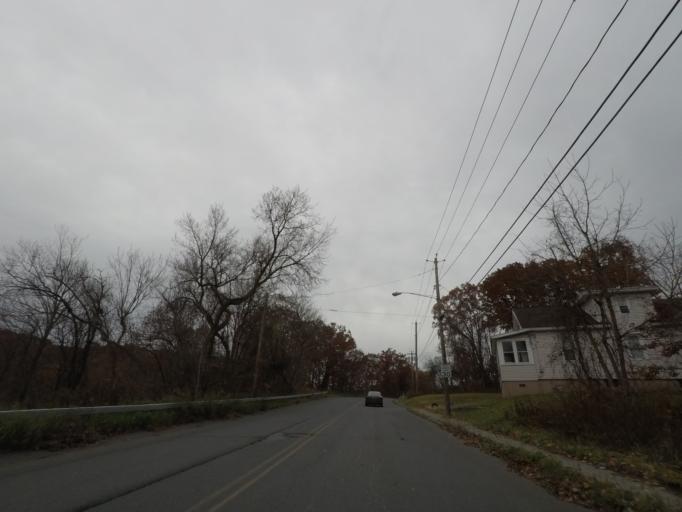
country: US
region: New York
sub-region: Rensselaer County
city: Troy
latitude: 42.7053
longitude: -73.6825
